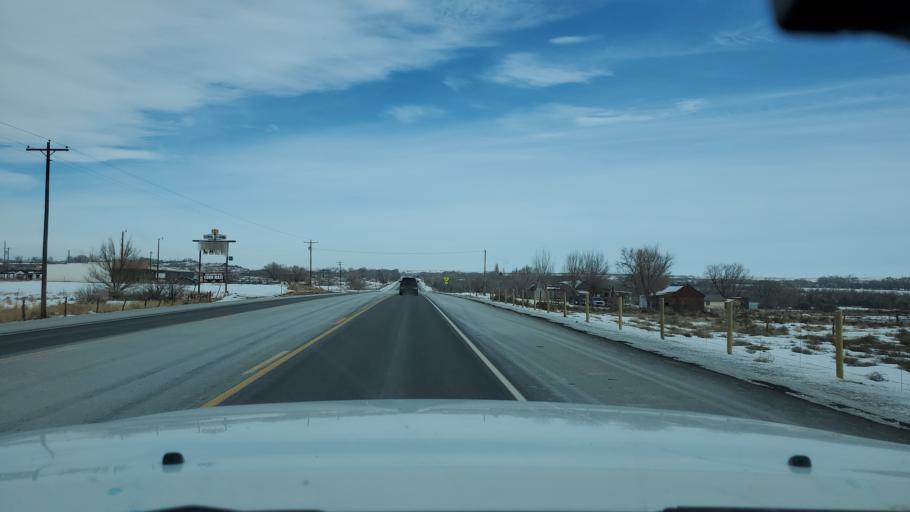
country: US
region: Utah
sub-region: Duchesne County
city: Roosevelt
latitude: 40.3019
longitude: -109.8336
